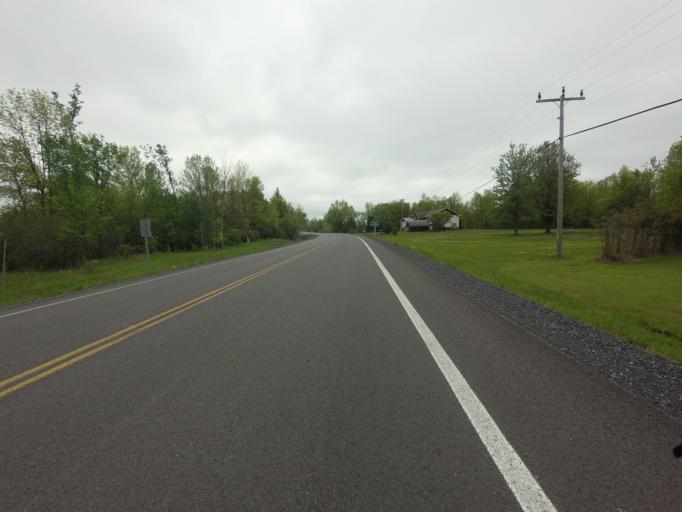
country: US
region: New York
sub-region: St. Lawrence County
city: Norfolk
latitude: 44.9418
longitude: -75.1484
